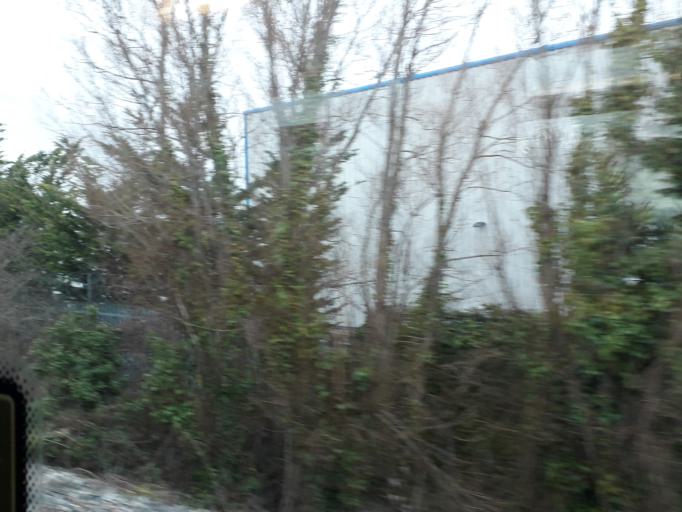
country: IE
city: Bayside
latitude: 53.3921
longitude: -6.1494
